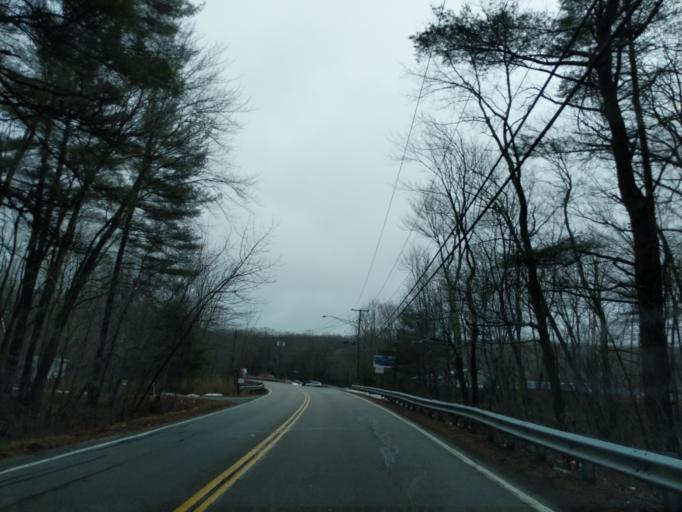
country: US
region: Massachusetts
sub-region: Worcester County
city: Webster
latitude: 42.0543
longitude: -71.8330
